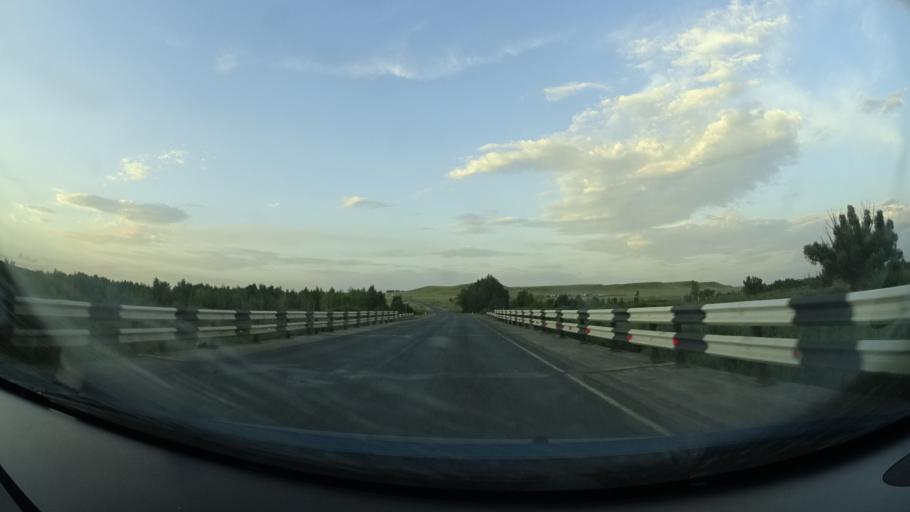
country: RU
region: Orenburg
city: Severnoye
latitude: 54.1331
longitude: 52.5910
